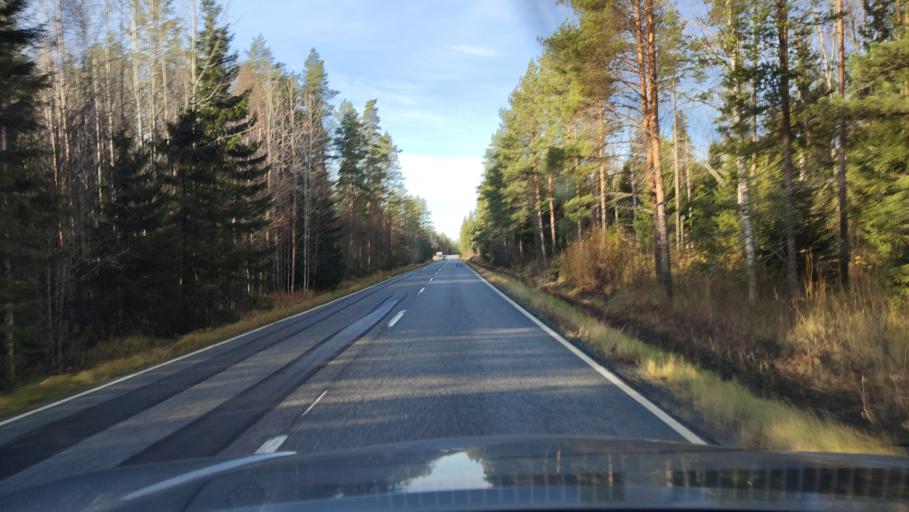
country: FI
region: Southern Ostrobothnia
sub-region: Suupohja
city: Teuva
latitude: 62.4592
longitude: 21.5620
